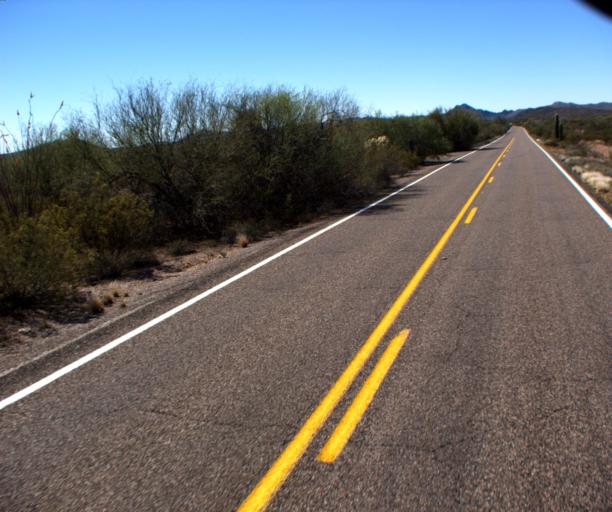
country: MX
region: Sonora
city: Sonoyta
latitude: 32.0310
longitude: -112.7991
